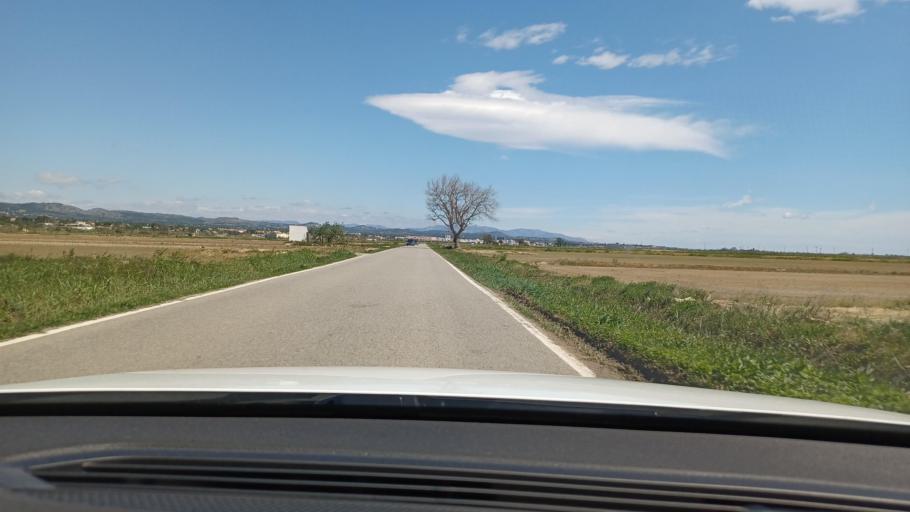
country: ES
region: Catalonia
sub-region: Provincia de Tarragona
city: L'Ampolla
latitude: 40.7833
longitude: 0.6917
